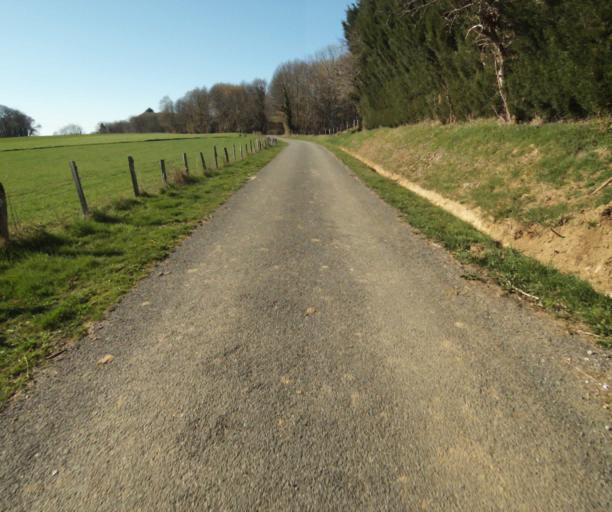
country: FR
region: Limousin
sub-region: Departement de la Correze
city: Chamboulive
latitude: 45.3989
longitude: 1.6674
